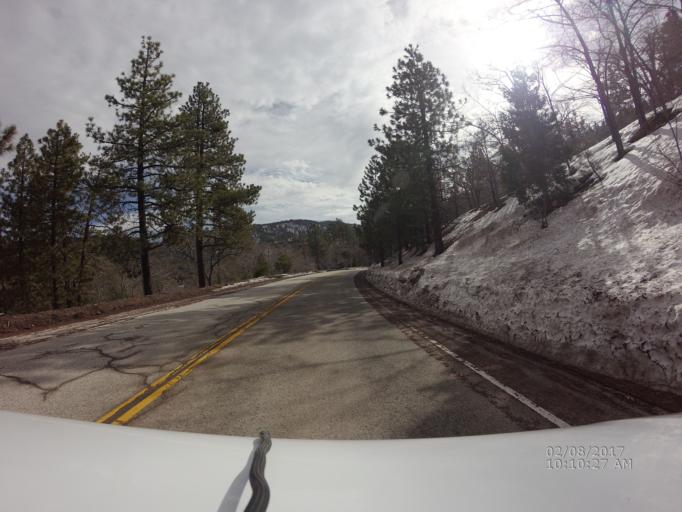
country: US
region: California
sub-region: San Bernardino County
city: Pinon Hills
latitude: 34.3915
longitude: -117.7226
